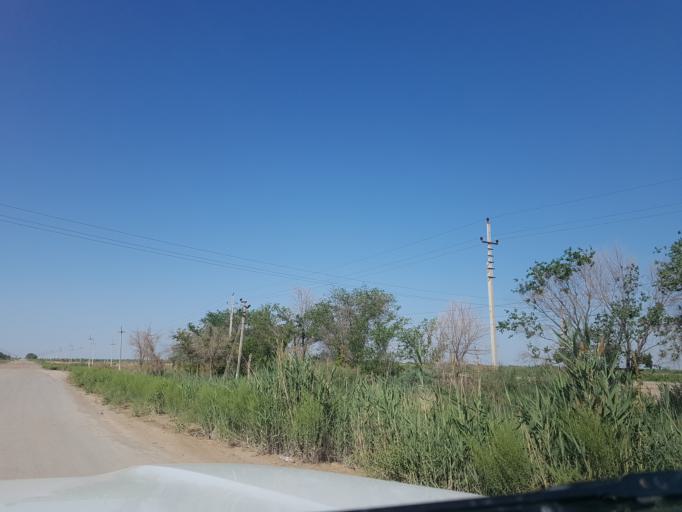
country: TM
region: Dasoguz
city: Koeneuergench
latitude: 42.1358
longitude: 58.9536
